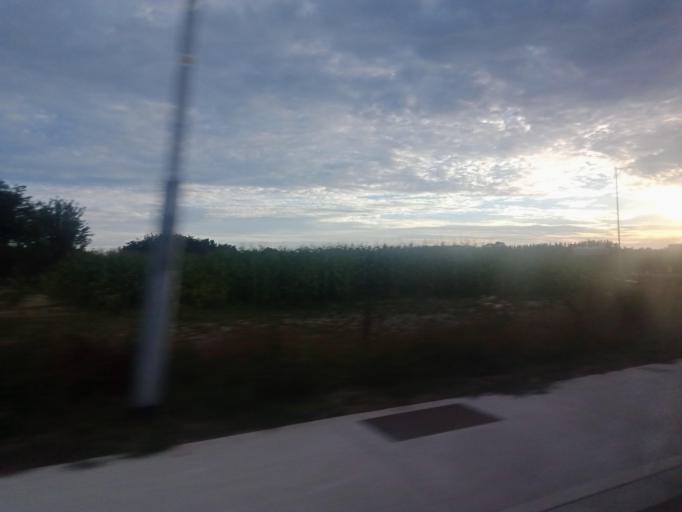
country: IE
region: Leinster
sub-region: Laois
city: Portlaoise
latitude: 53.0153
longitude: -7.3119
